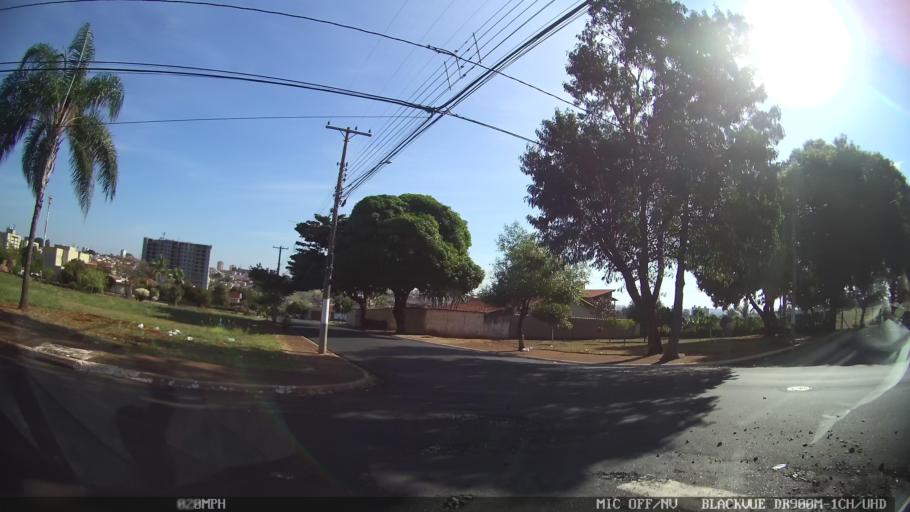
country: BR
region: Sao Paulo
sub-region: Ribeirao Preto
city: Ribeirao Preto
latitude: -21.1762
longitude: -47.7760
